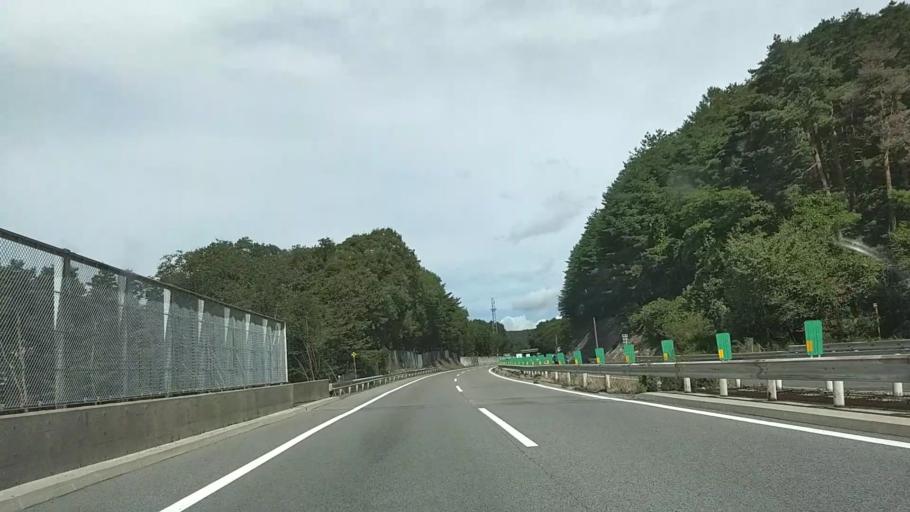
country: JP
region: Nagano
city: Chino
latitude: 35.8736
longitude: 138.3067
